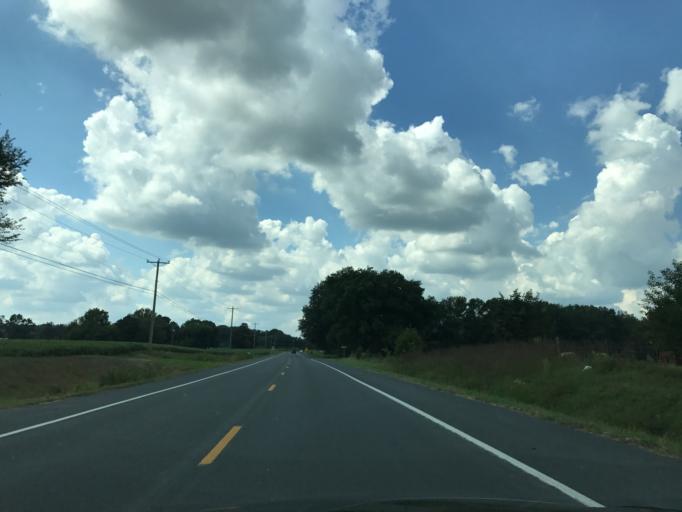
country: US
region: Maryland
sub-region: Caroline County
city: Greensboro
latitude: 39.1336
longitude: -75.7850
